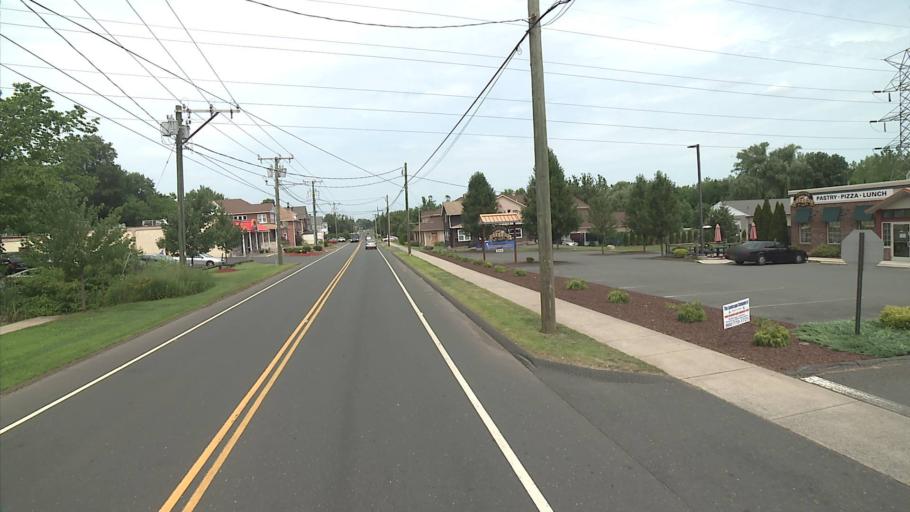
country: US
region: Connecticut
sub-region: Hartford County
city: Kensington
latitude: 41.6414
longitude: -72.7700
